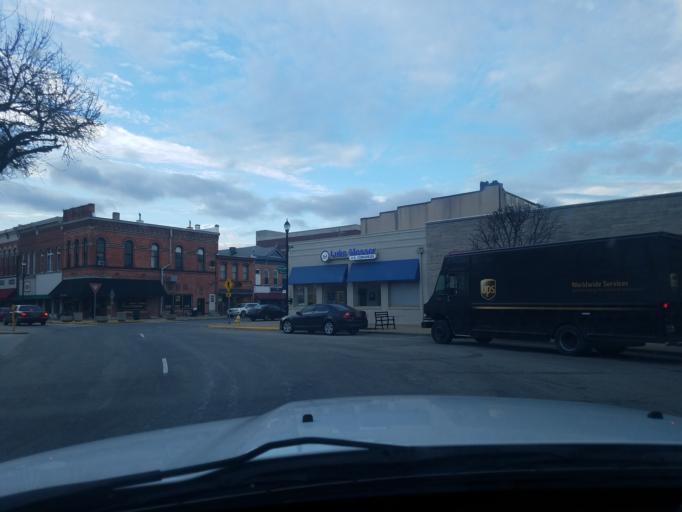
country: US
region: Indiana
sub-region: Shelby County
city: Shelbyville
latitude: 39.5245
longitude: -85.7766
